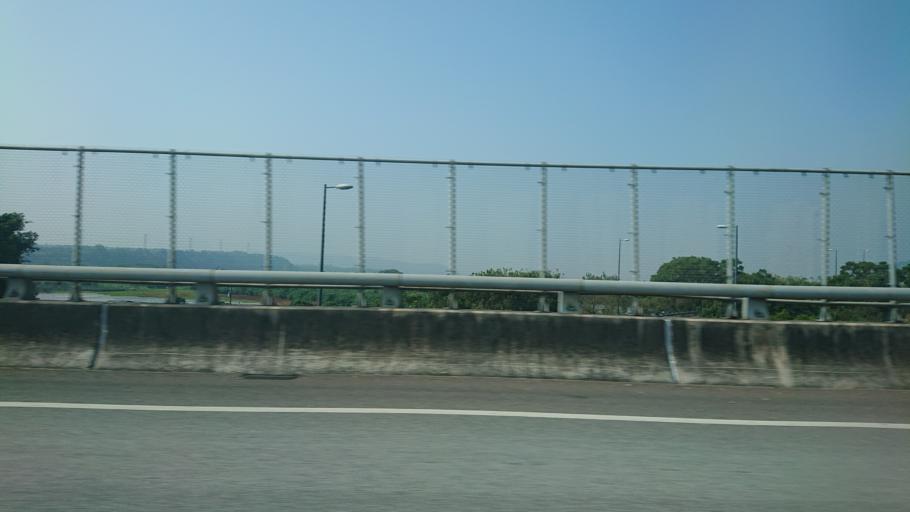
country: TW
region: Taiwan
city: Lugu
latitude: 23.7959
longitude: 120.7018
